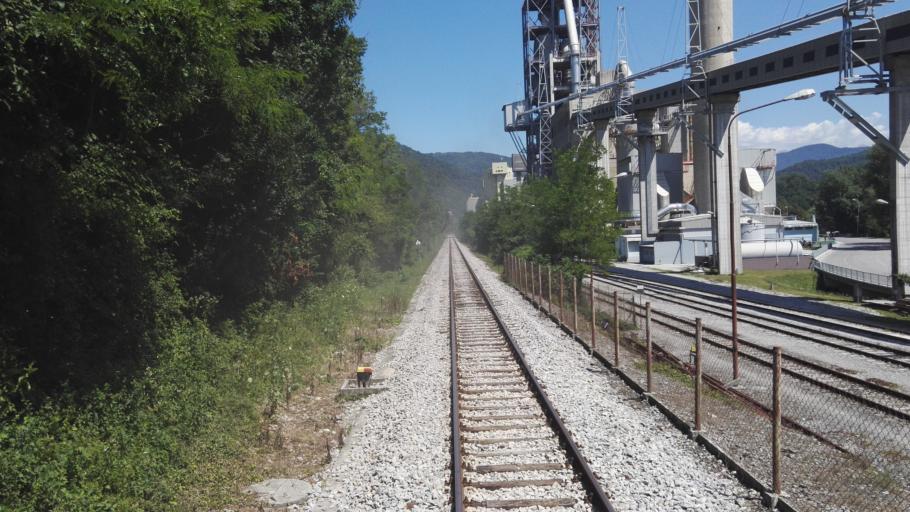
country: SI
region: Kanal
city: Deskle
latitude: 46.0657
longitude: 13.6271
